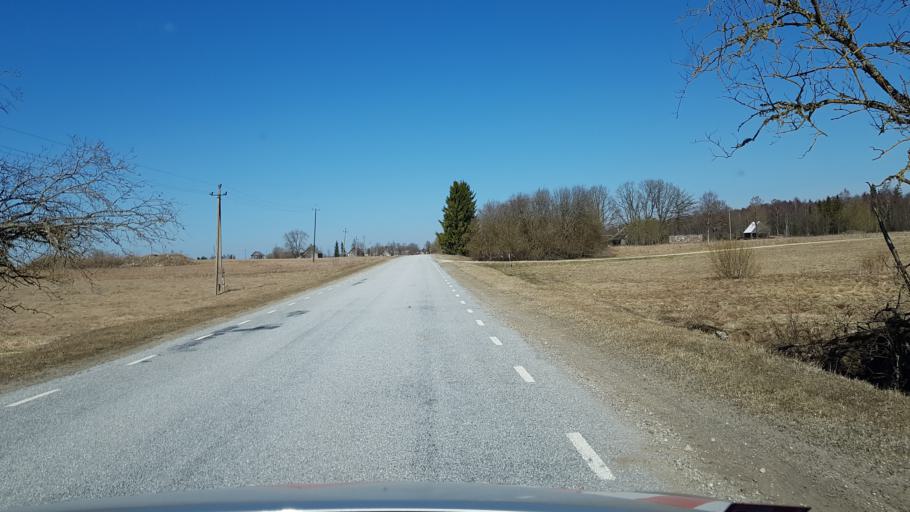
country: EE
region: Jaervamaa
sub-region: Koeru vald
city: Koeru
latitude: 59.0418
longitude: 26.0914
